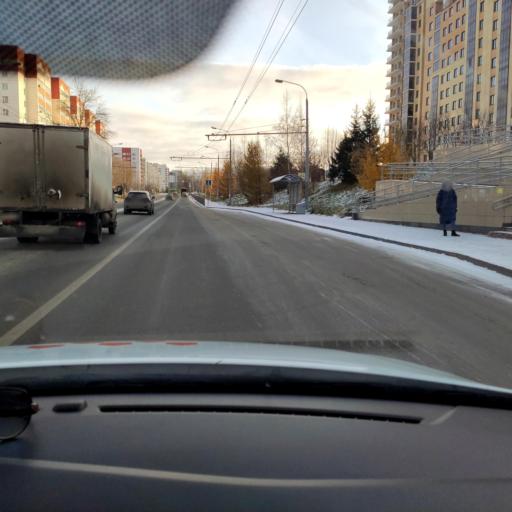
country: RU
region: Tatarstan
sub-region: Gorod Kazan'
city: Kazan
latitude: 55.7440
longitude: 49.1871
